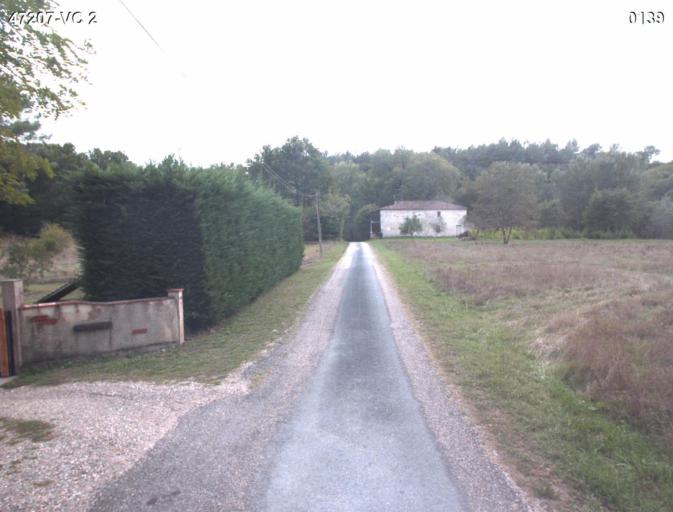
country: FR
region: Aquitaine
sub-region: Departement du Lot-et-Garonne
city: Barbaste
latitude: 44.1791
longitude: 0.2220
